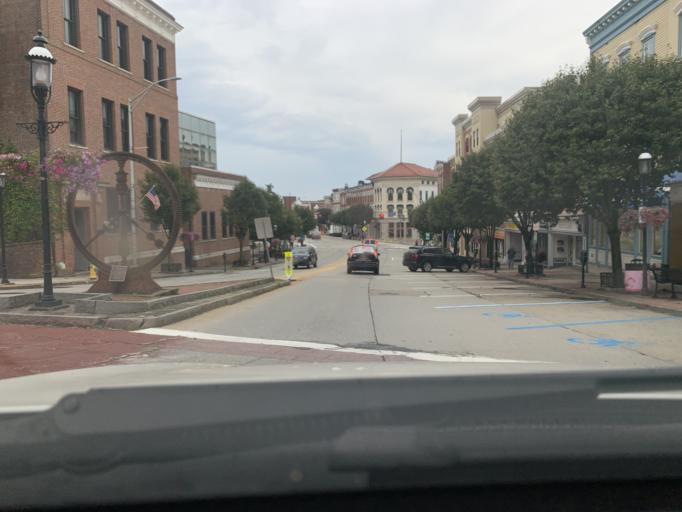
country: US
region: New York
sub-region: Westchester County
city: Ossining
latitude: 41.1614
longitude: -73.8624
